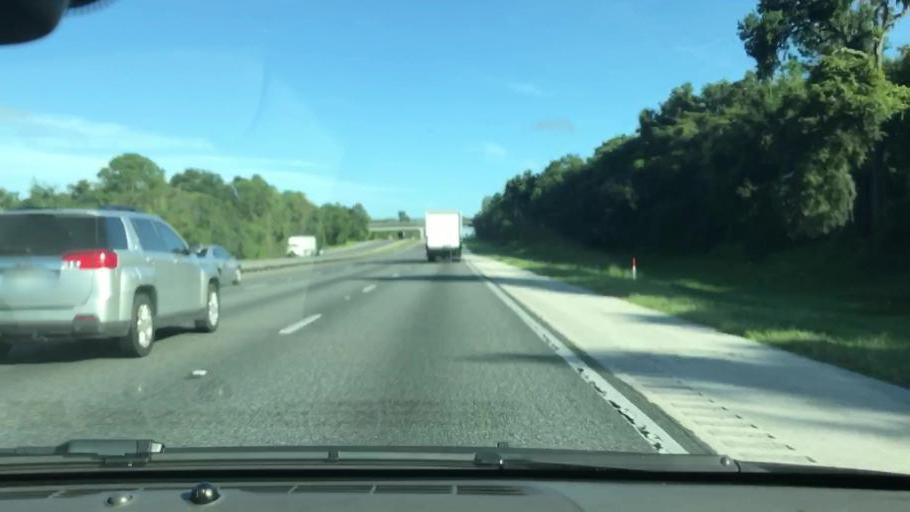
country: US
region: Florida
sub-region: Marion County
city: Belleview
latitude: 29.0484
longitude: -82.1665
